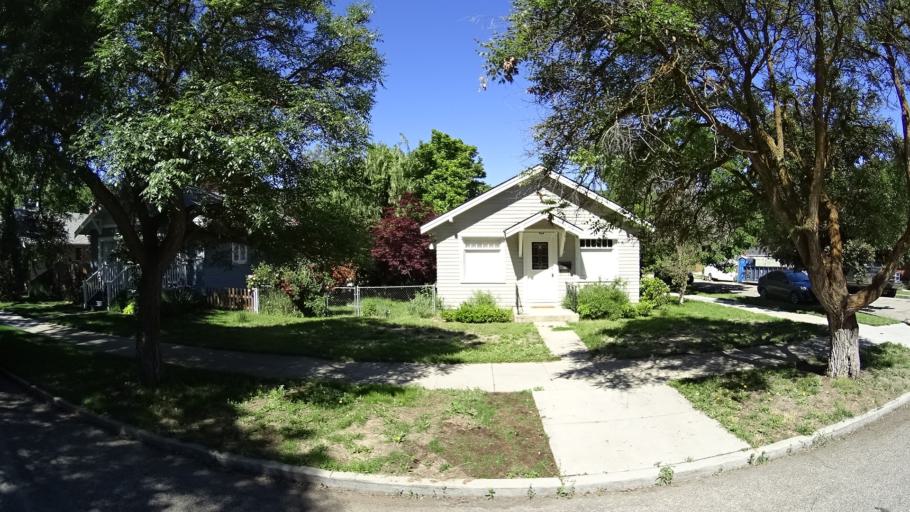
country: US
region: Idaho
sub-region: Ada County
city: Boise
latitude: 43.6354
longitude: -116.2134
